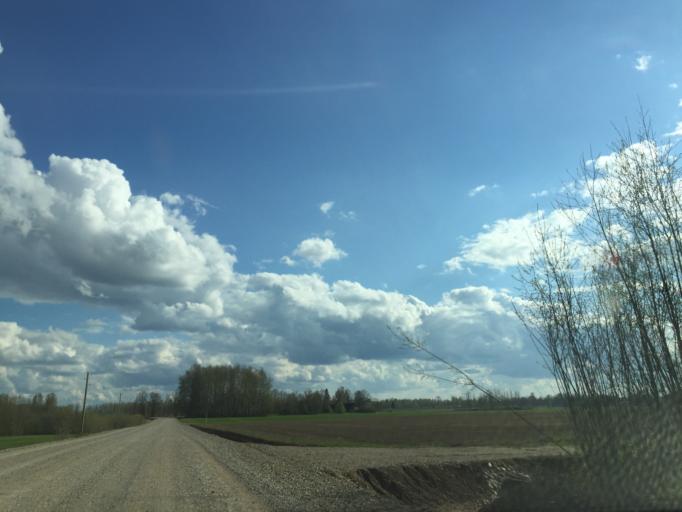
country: LV
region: Beverina
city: Murmuiza
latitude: 57.4079
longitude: 25.5106
